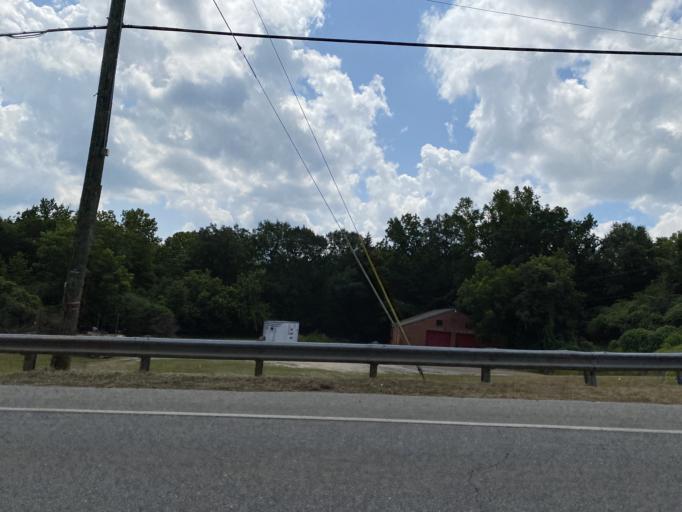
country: US
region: Alabama
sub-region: Wilcox County
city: Camden
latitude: 31.9917
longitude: -87.2875
